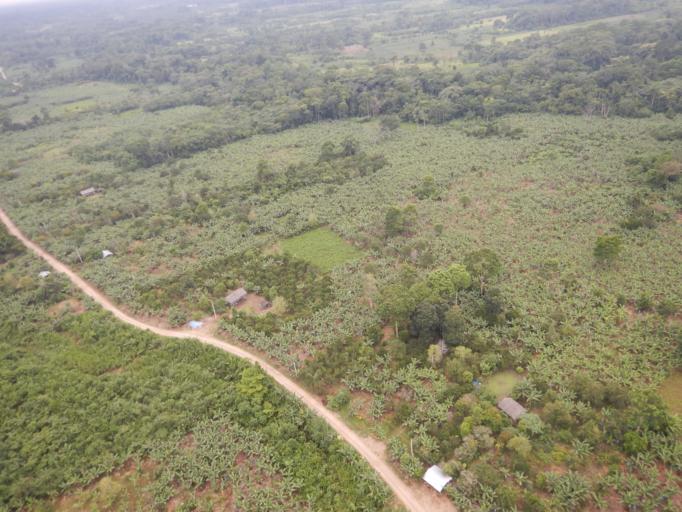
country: BO
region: Cochabamba
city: Chimore
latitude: -17.1398
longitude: -64.8097
